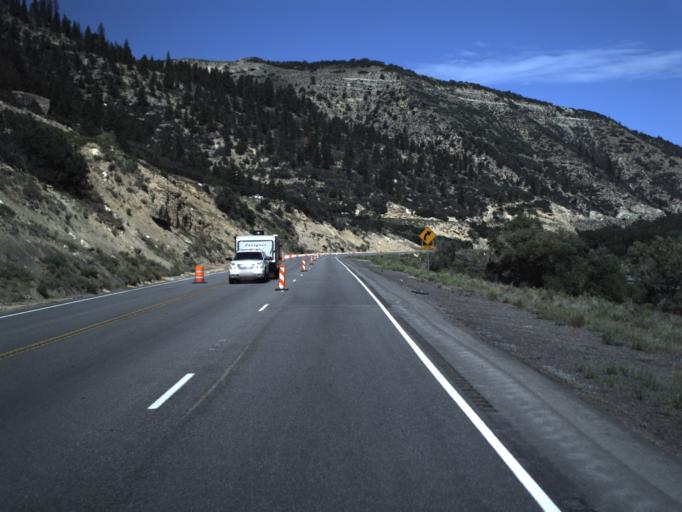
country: US
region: Utah
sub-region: Carbon County
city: Helper
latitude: 39.7840
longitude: -110.9242
